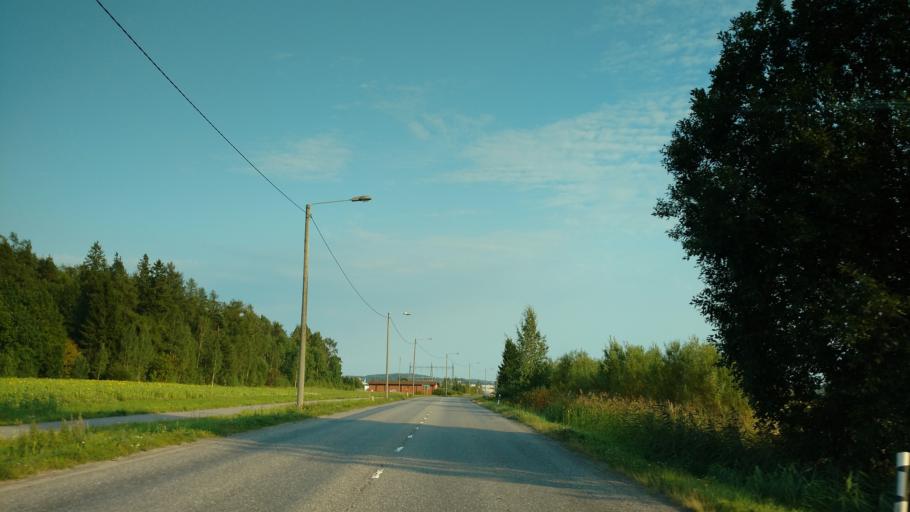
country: FI
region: Varsinais-Suomi
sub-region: Salo
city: Halikko
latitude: 60.3905
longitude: 23.0931
